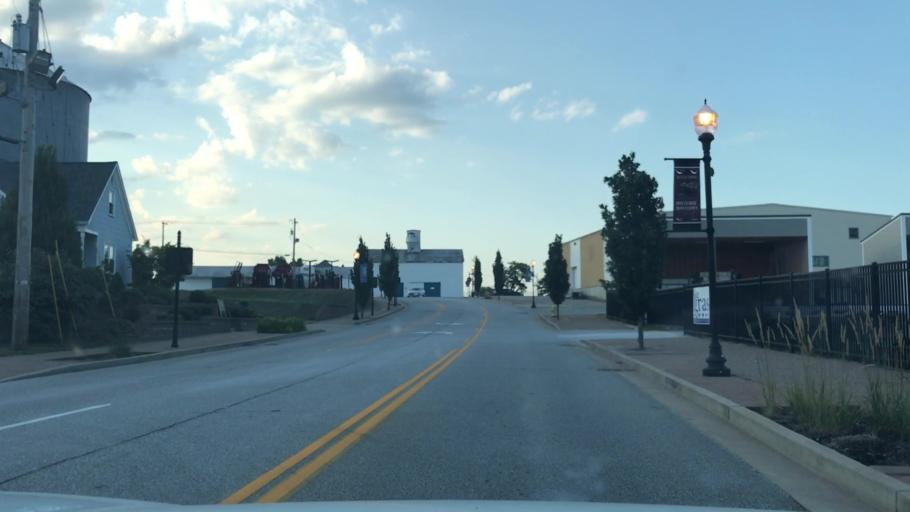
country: US
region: Missouri
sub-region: Saint Charles County
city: Wentzville
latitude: 38.8096
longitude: -90.8539
